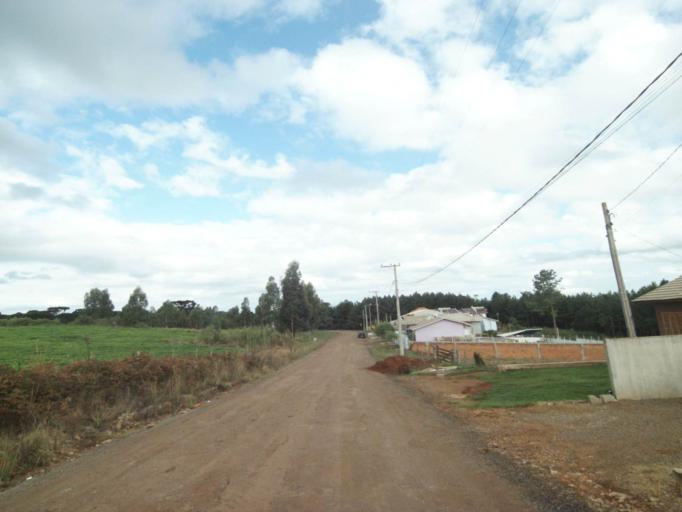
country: BR
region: Rio Grande do Sul
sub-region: Lagoa Vermelha
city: Lagoa Vermelha
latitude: -28.2047
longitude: -51.5115
